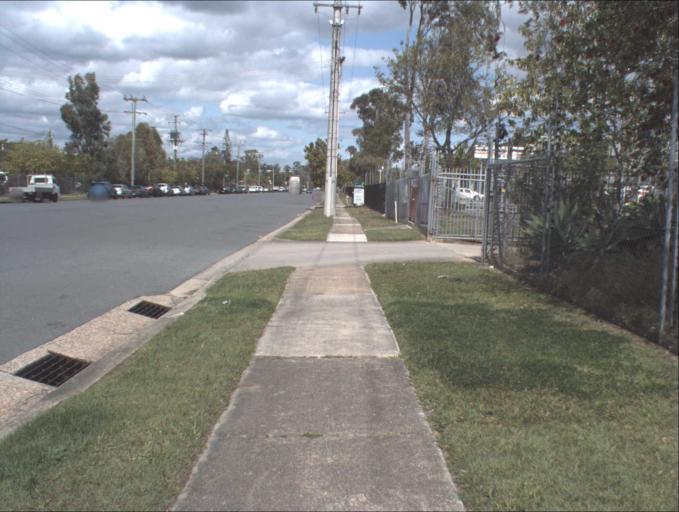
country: AU
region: Queensland
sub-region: Logan
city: Logan Reserve
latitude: -27.6801
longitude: 153.0784
